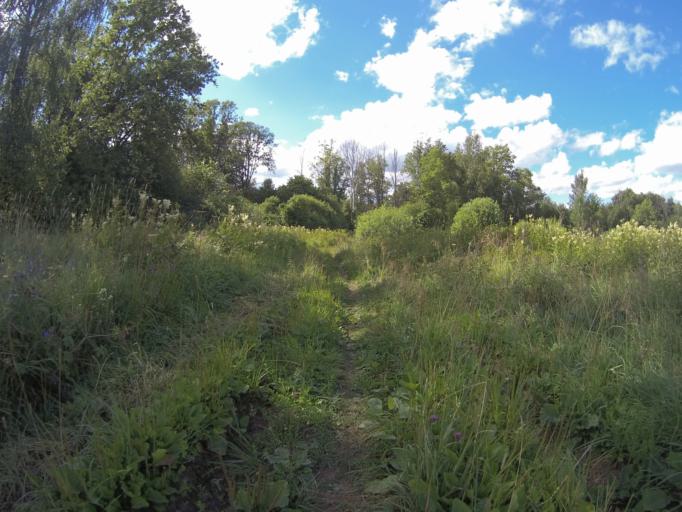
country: RU
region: Vladimir
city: Vladimir
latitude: 56.0739
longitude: 40.3841
